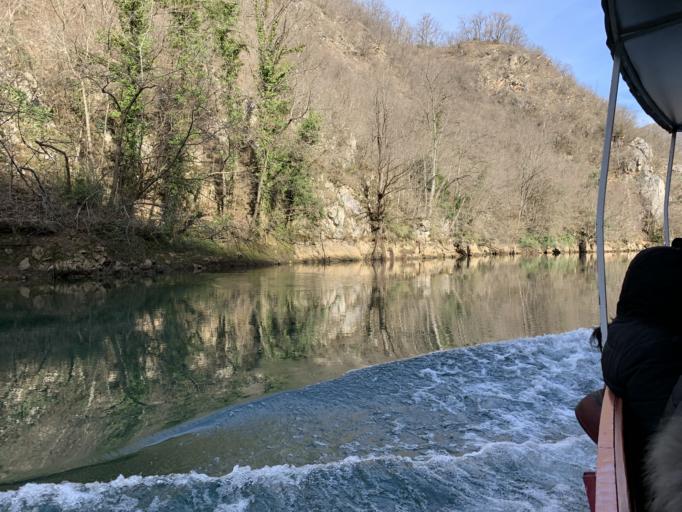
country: MK
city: Bukovik
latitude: 41.9311
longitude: 21.2933
